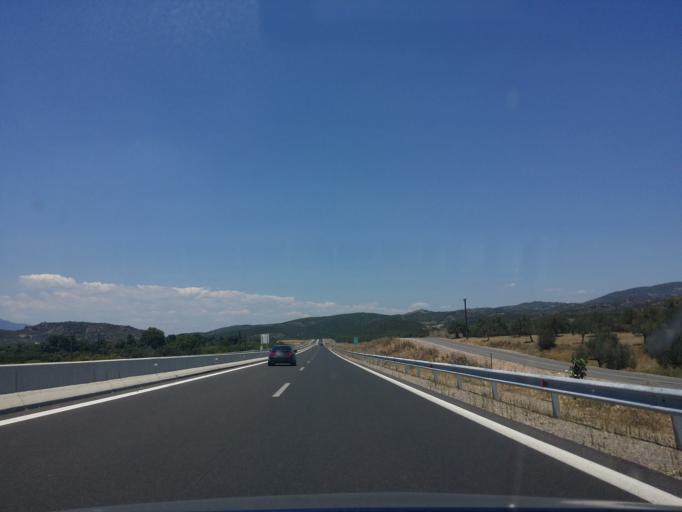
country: GR
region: Peloponnese
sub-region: Nomos Lakonias
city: Sparti
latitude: 37.1029
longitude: 22.4250
